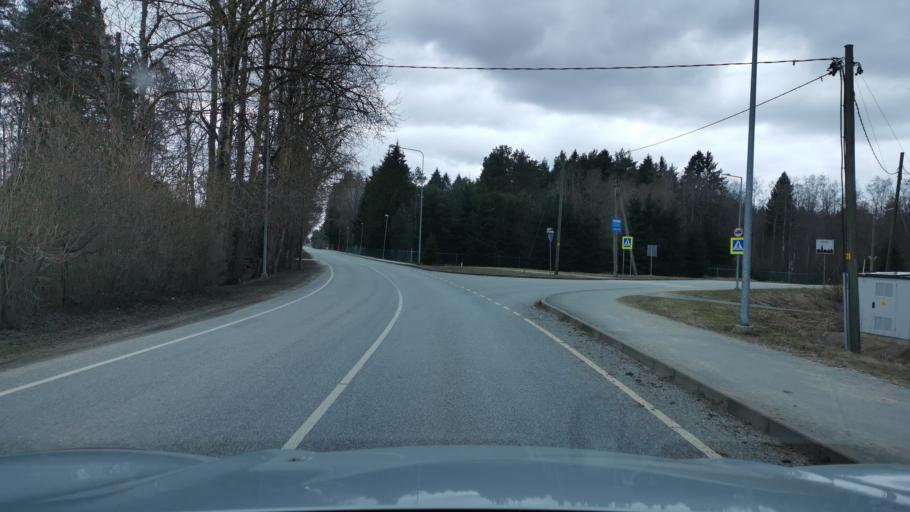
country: EE
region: Ida-Virumaa
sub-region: Puessi linn
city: Pussi
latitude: 59.3682
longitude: 27.0475
